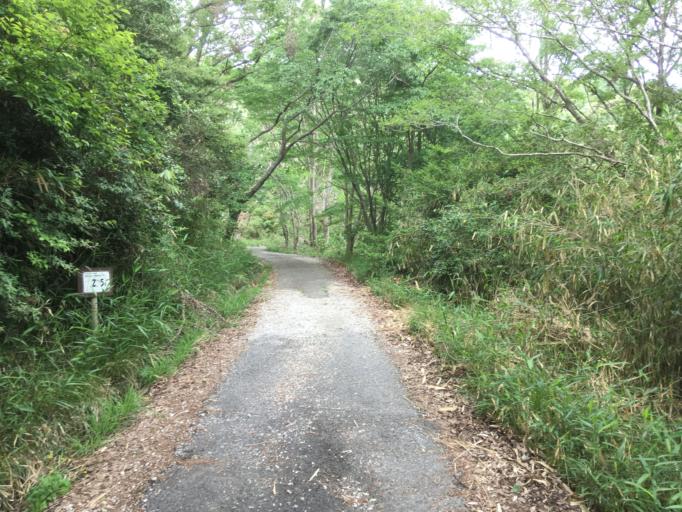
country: JP
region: Nara
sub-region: Ikoma-shi
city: Ikoma
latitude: 34.6867
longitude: 135.6721
